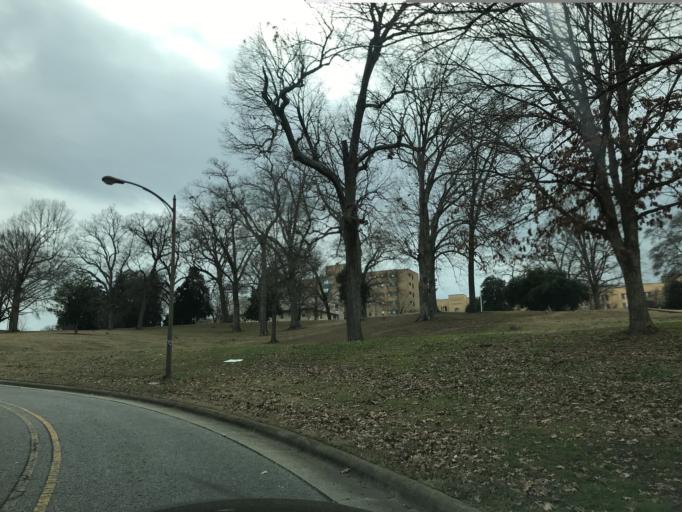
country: US
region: North Carolina
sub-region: Wake County
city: Raleigh
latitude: 35.7710
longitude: -78.6538
